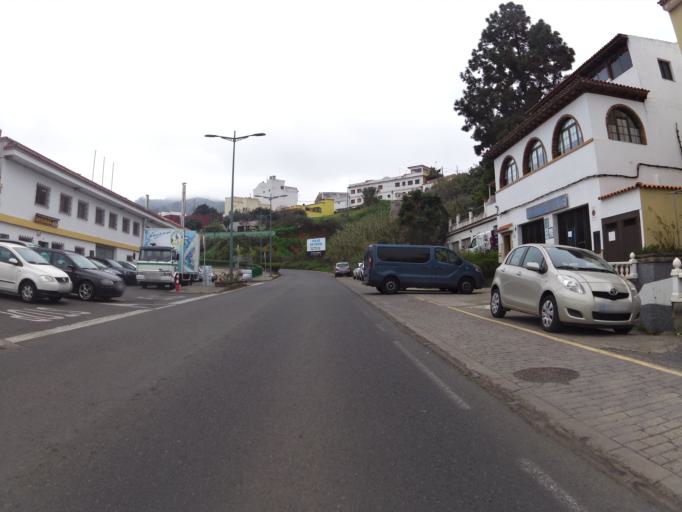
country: ES
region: Canary Islands
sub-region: Provincia de Las Palmas
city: Teror
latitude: 28.0629
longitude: -15.5397
